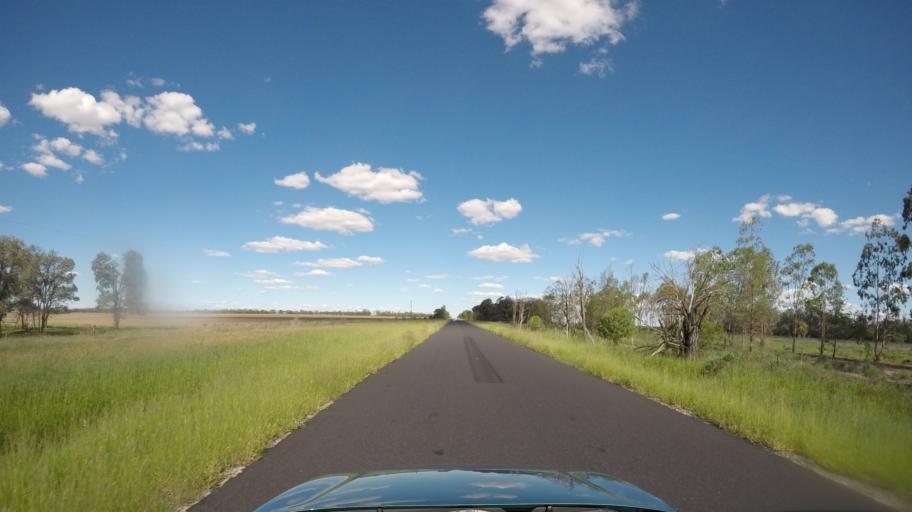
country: AU
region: Queensland
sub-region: Goondiwindi
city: Goondiwindi
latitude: -28.1657
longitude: 150.1751
